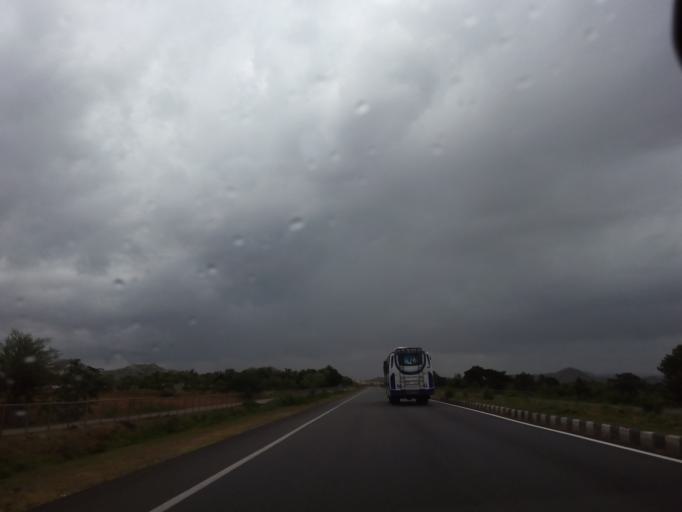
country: IN
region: Karnataka
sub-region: Chitradurga
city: Chitradurga
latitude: 14.2690
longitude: 76.3314
